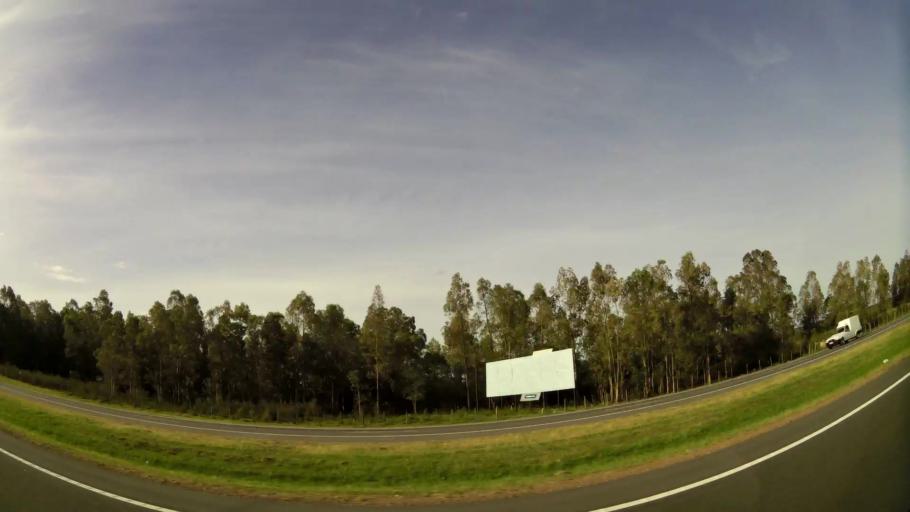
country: UY
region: Canelones
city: La Floresta
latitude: -34.7542
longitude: -55.6048
